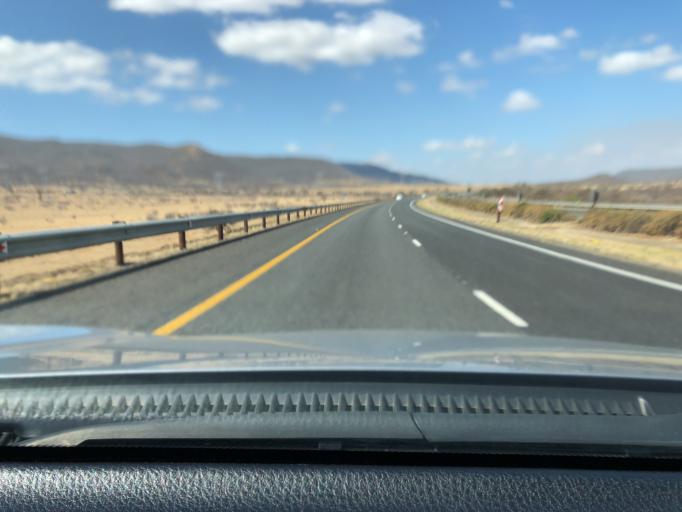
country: ZA
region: KwaZulu-Natal
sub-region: uThukela District Municipality
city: Ladysmith
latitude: -28.6931
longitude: 29.6381
